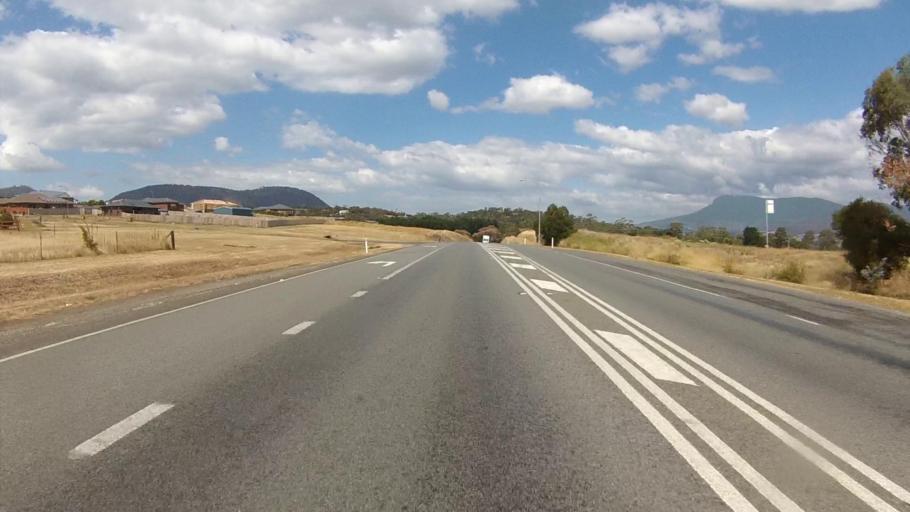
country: AU
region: Tasmania
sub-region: Brighton
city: Old Beach
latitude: -42.7617
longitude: 147.2688
